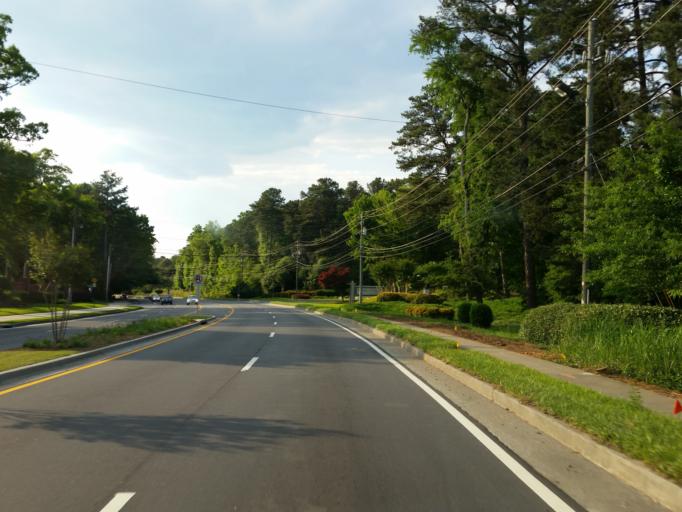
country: US
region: Georgia
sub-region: Cobb County
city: Smyrna
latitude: 33.8691
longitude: -84.4943
